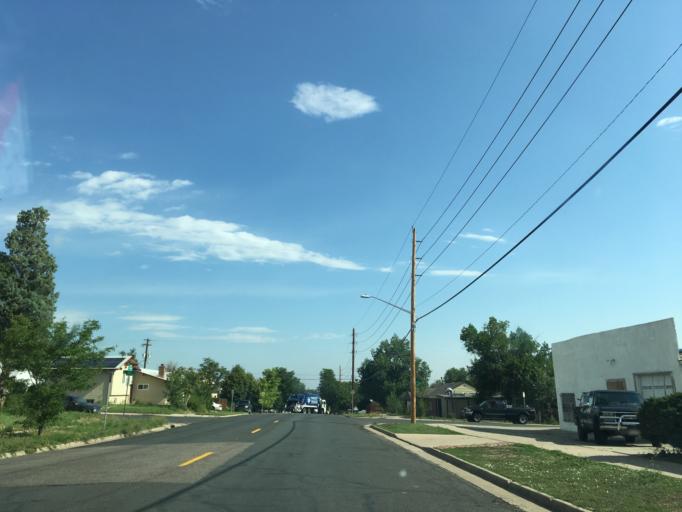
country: US
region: Colorado
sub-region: Jefferson County
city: Lakewood
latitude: 39.7044
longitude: -105.0298
